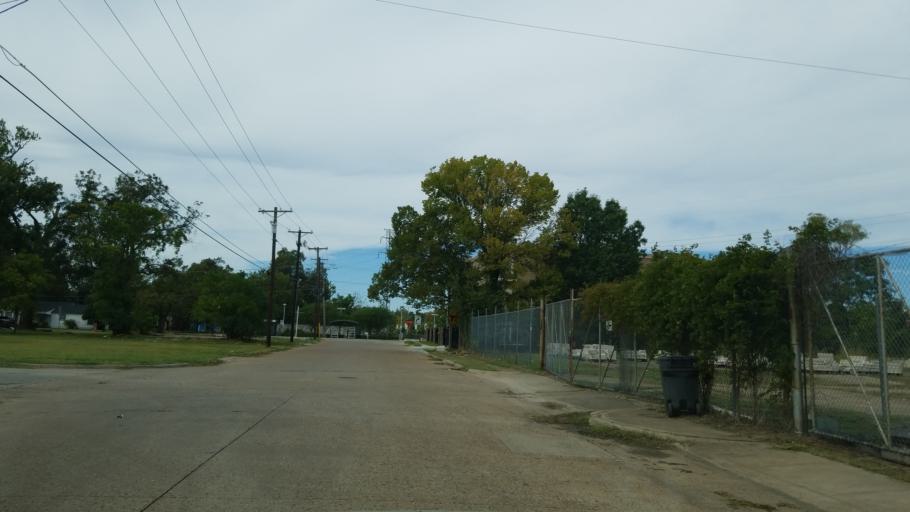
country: US
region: Texas
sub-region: Dallas County
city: Dallas
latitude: 32.7651
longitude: -96.7405
